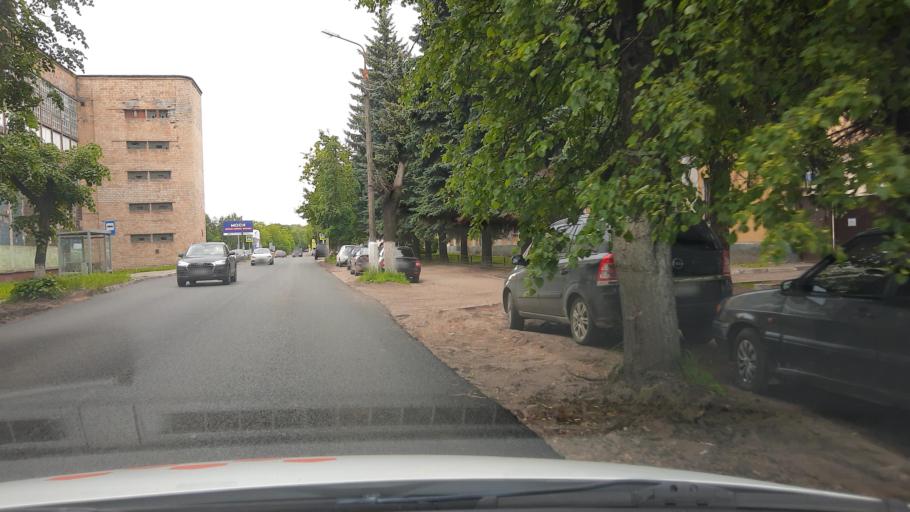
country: RU
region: Moskovskaya
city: Noginsk
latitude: 55.8744
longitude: 38.4524
